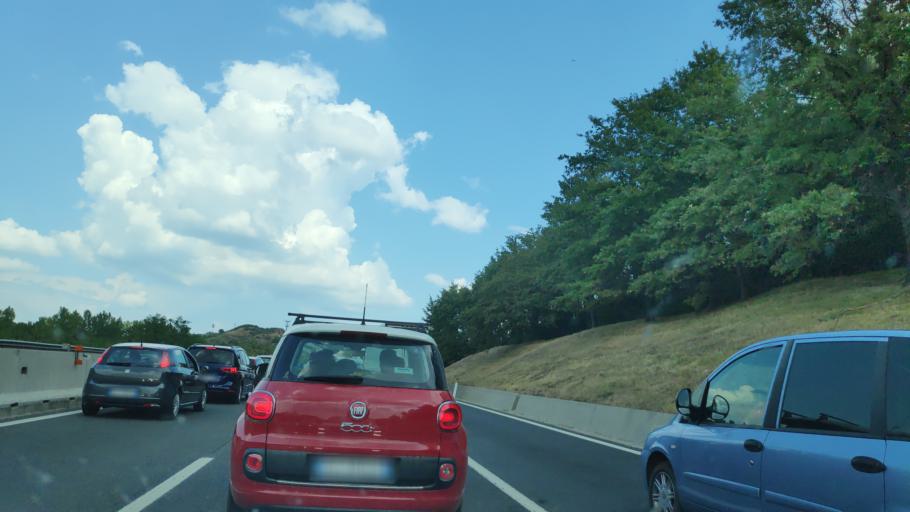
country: IT
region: Umbria
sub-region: Provincia di Terni
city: Ficulle
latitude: 42.8253
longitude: 12.0413
